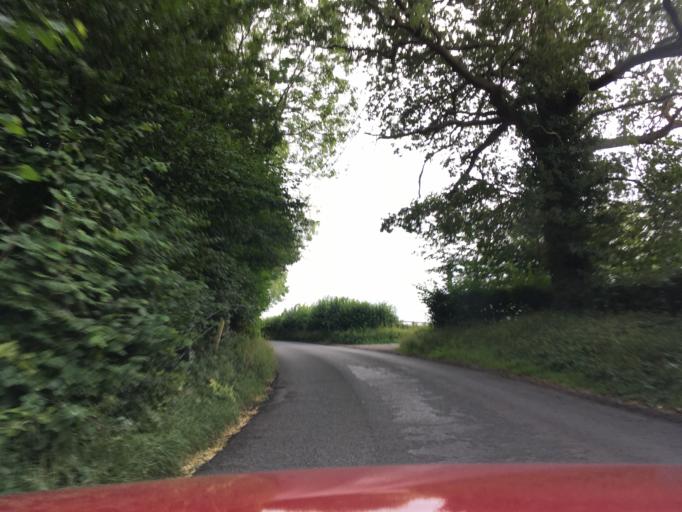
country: GB
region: England
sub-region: Hampshire
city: Colden Common
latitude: 50.9985
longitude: -1.2735
